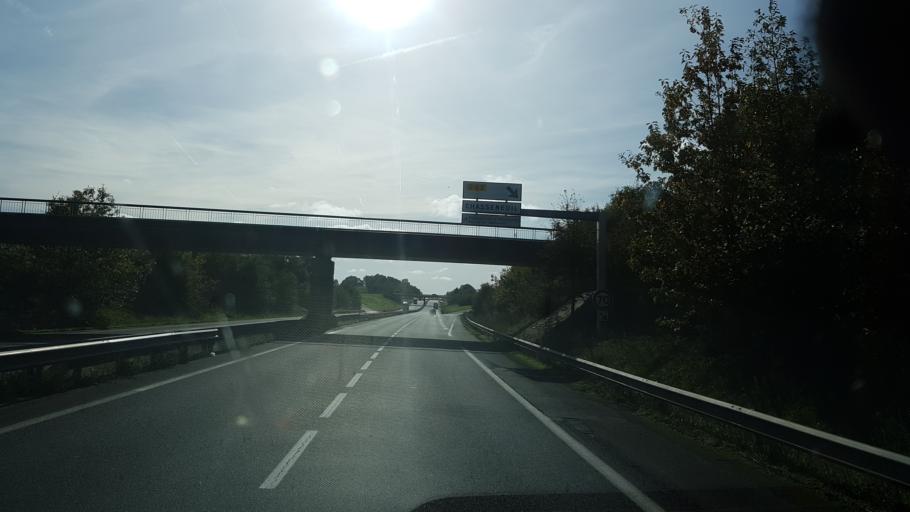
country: FR
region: Poitou-Charentes
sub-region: Departement de la Charente
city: Chasseneuil-sur-Bonnieure
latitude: 45.8161
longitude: 0.4542
